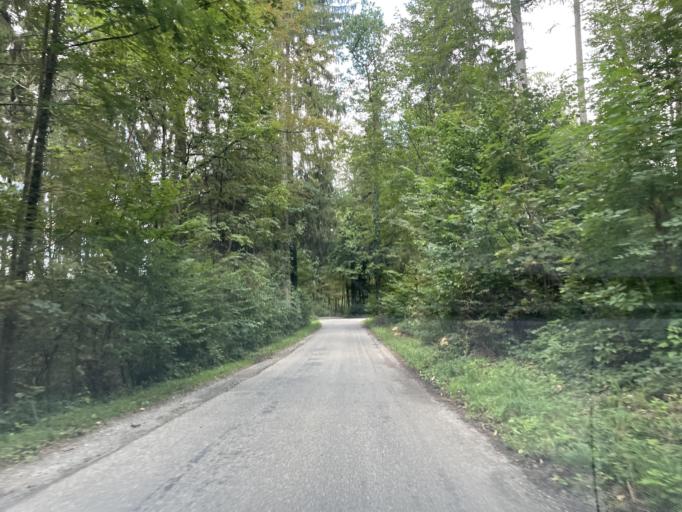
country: CH
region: Zurich
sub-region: Bezirk Winterthur
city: Seen (Kreis 3) / Ganzenbuehl
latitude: 47.4742
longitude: 8.7575
